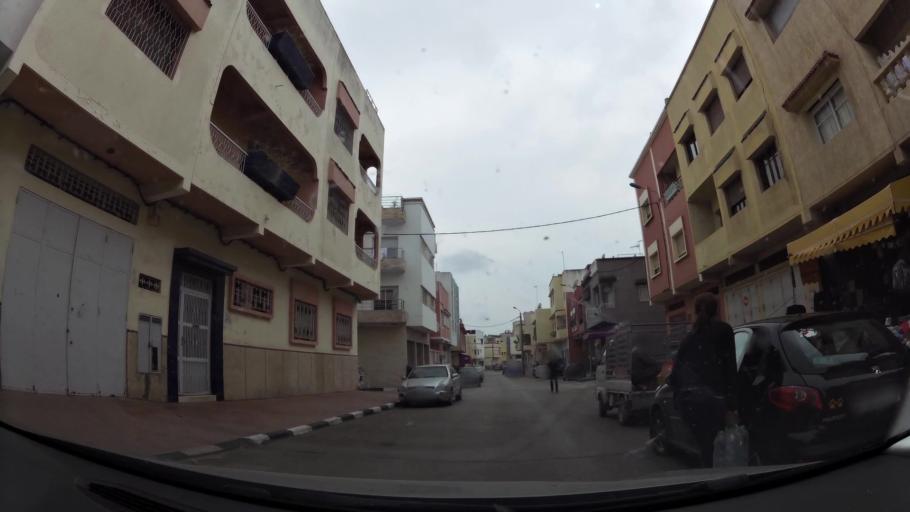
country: MA
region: Rabat-Sale-Zemmour-Zaer
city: Sale
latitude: 34.0285
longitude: -6.8021
